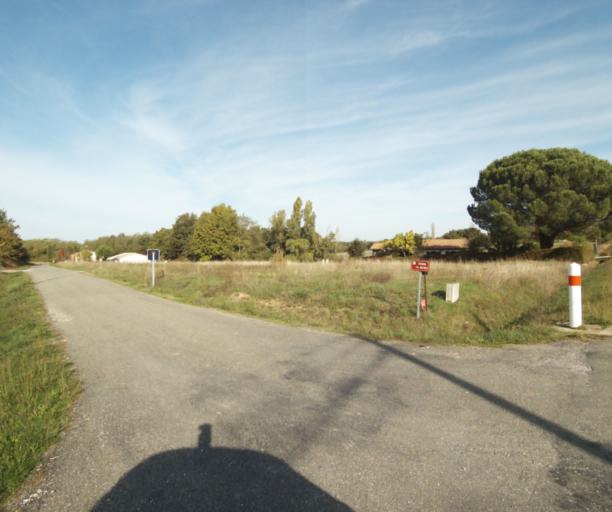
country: FR
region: Midi-Pyrenees
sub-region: Departement du Tarn-et-Garonne
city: Nohic
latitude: 43.9274
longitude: 1.4640
